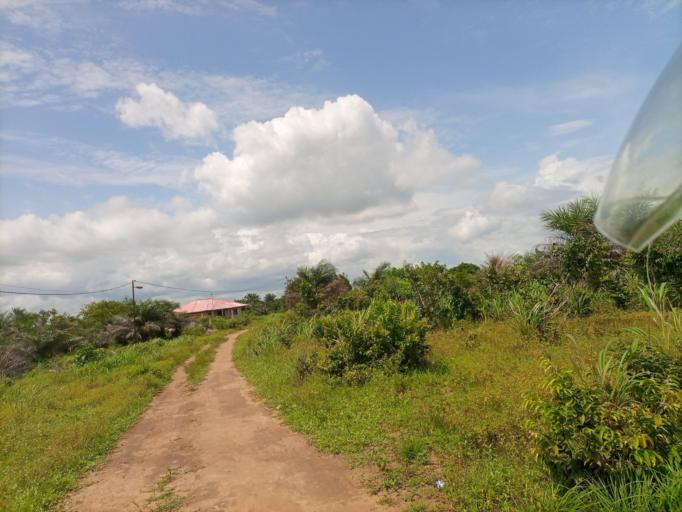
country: SL
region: Northern Province
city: Masoyila
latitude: 8.5410
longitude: -13.1483
